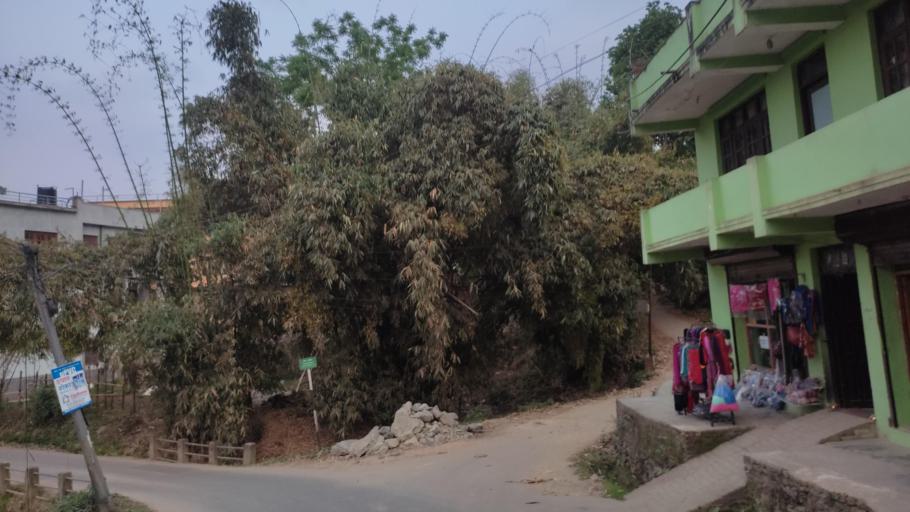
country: NP
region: Central Region
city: Kirtipur
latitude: 27.6668
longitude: 85.2505
